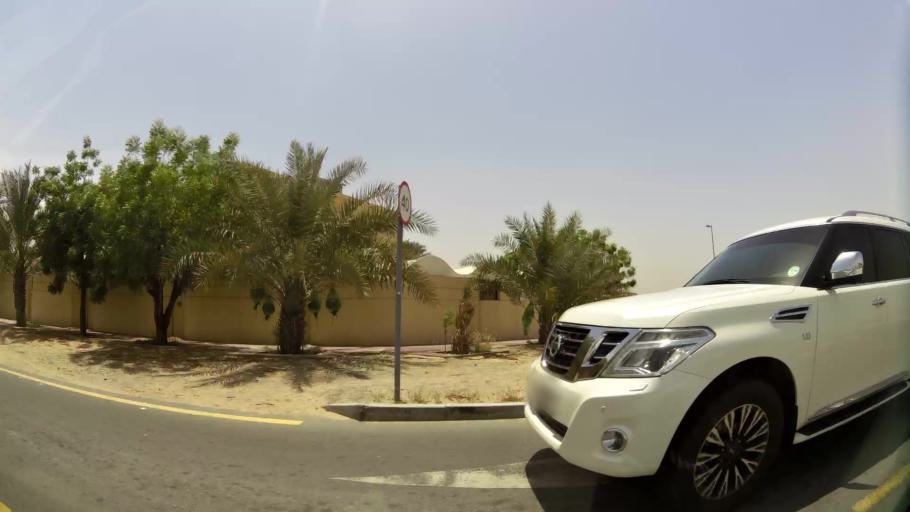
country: AE
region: Ash Shariqah
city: Sharjah
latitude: 25.2359
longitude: 55.4840
